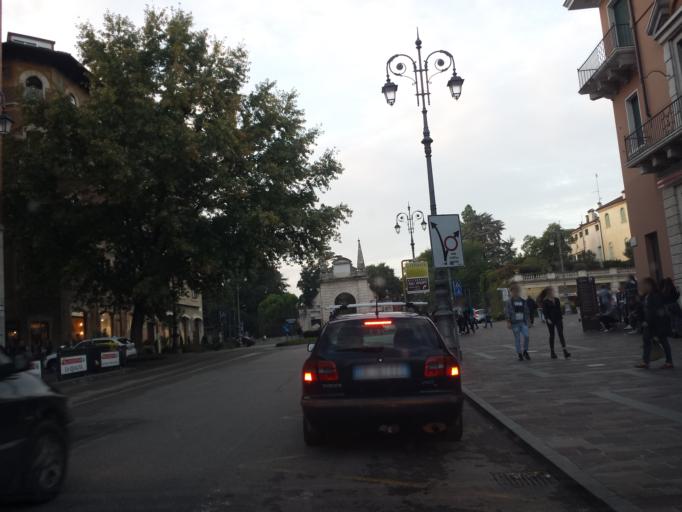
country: IT
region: Veneto
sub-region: Provincia di Vicenza
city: Vicenza
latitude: 45.5453
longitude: 11.5403
